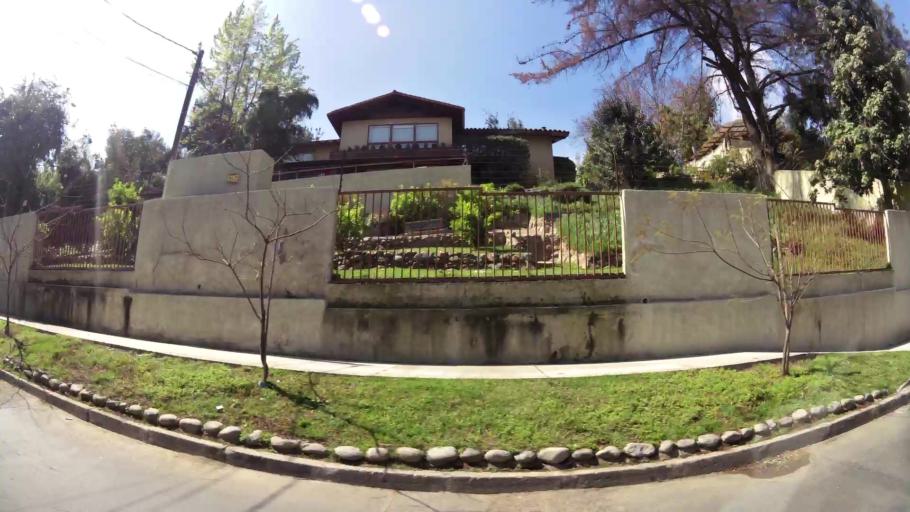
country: CL
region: Santiago Metropolitan
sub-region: Provincia de Santiago
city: Villa Presidente Frei, Nunoa, Santiago, Chile
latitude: -33.4475
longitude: -70.5232
